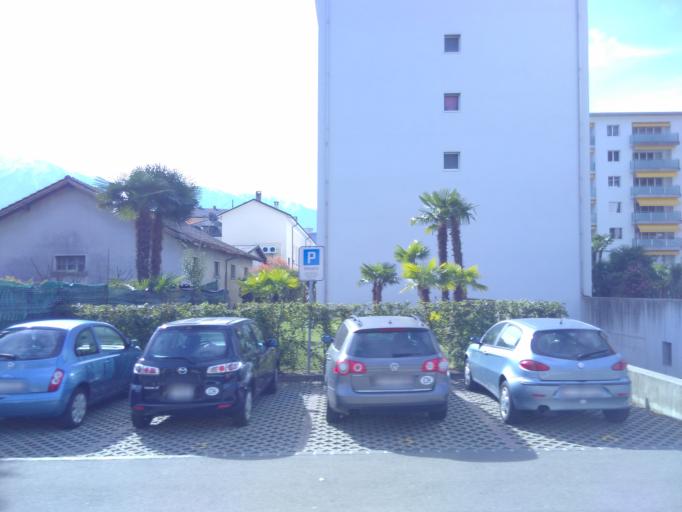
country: CH
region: Ticino
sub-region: Locarno District
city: Locarno
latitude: 46.1687
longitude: 8.7875
